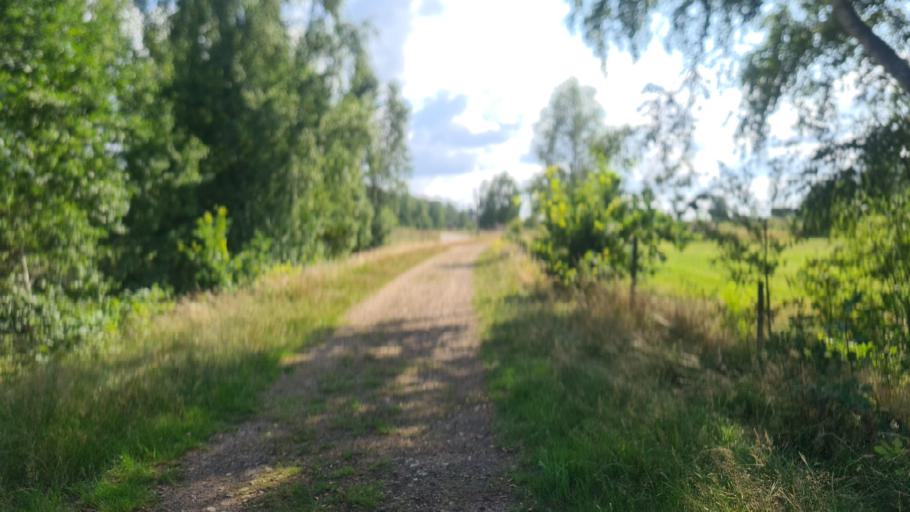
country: SE
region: Kronoberg
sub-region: Ljungby Kommun
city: Ljungby
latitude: 56.7774
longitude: 13.9028
